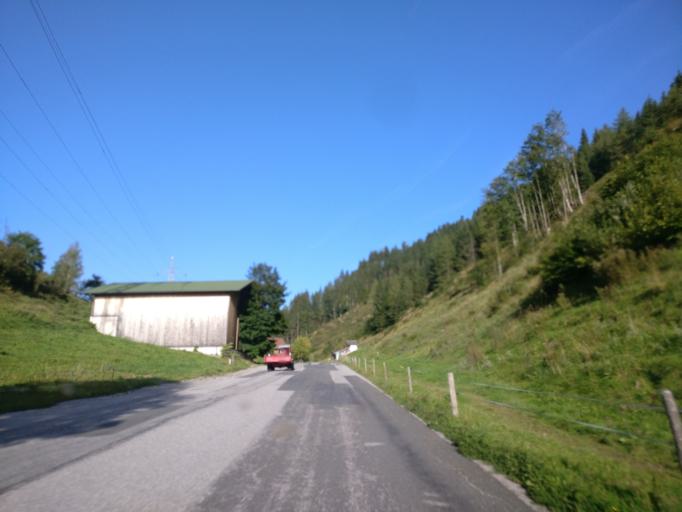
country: AT
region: Salzburg
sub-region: Politischer Bezirk Zell am See
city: Lend
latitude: 47.3151
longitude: 13.0483
